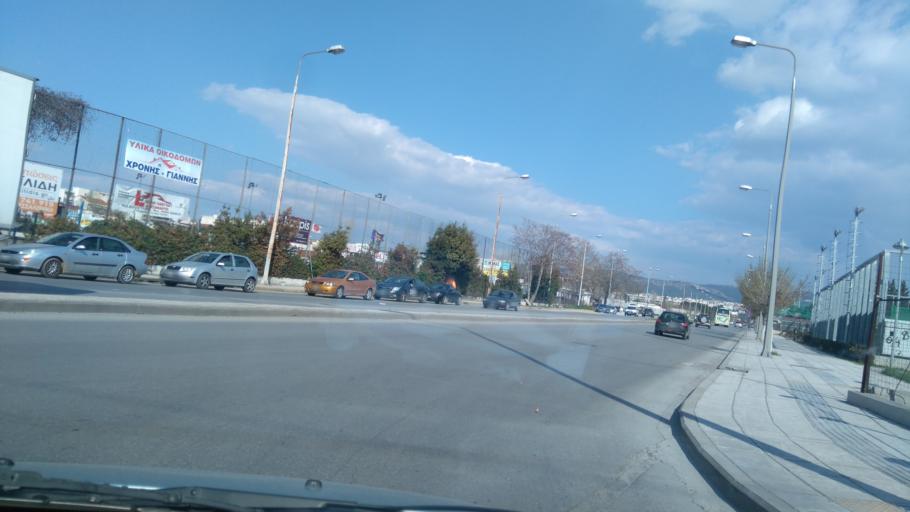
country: GR
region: Central Macedonia
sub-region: Nomos Thessalonikis
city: Evosmos
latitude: 40.6601
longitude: 22.9128
